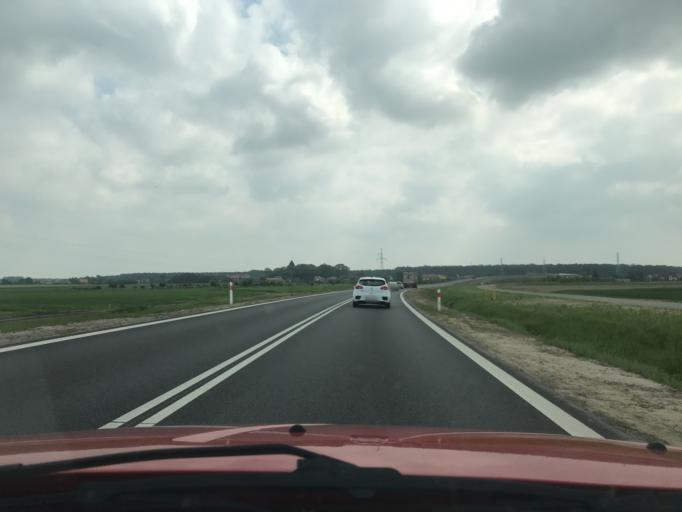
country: PL
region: Greater Poland Voivodeship
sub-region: Powiat jarocinski
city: Jarocin
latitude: 51.9750
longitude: 17.5257
